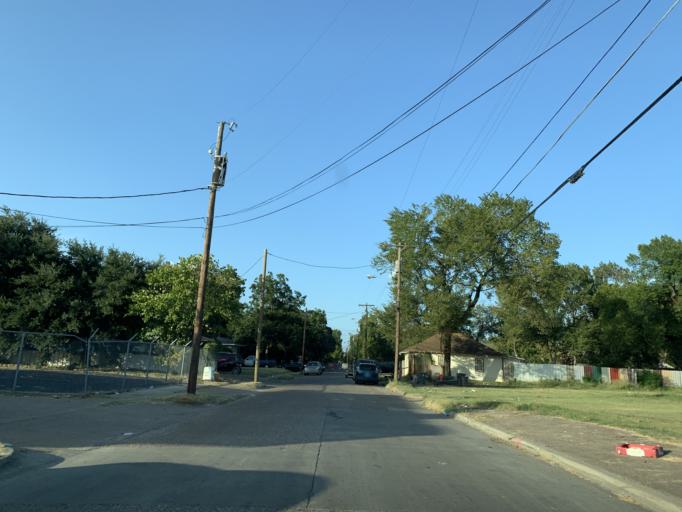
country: US
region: Texas
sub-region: Dallas County
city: Dallas
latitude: 32.7609
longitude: -96.7441
